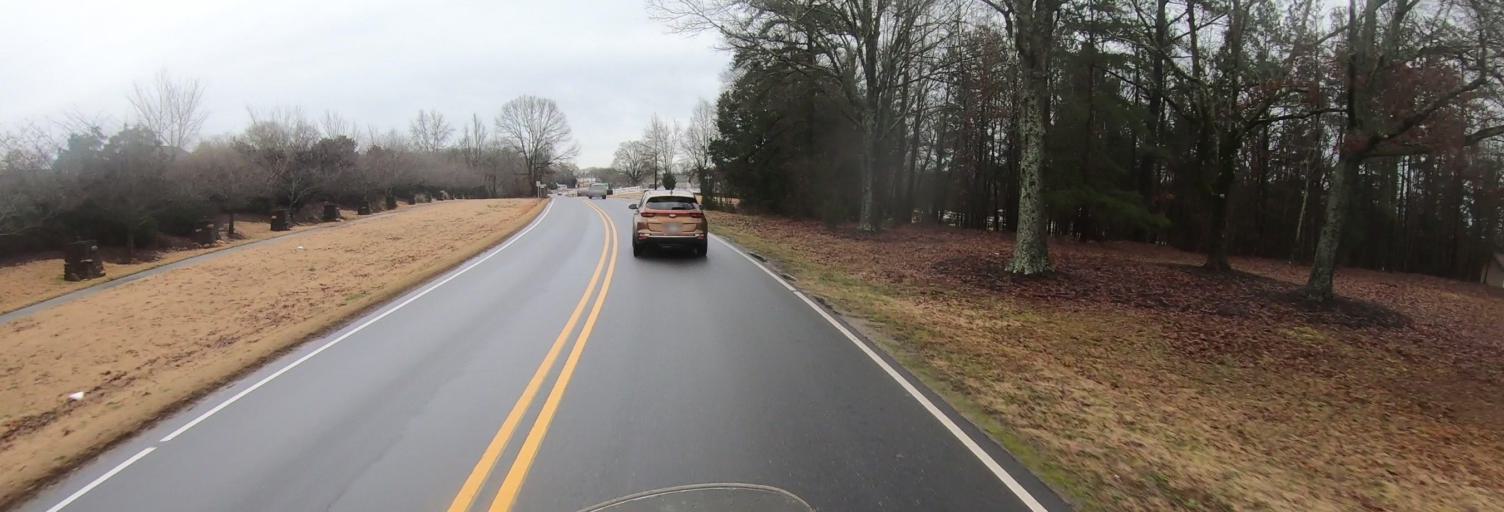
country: US
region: South Carolina
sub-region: York County
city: Tega Cay
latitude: 35.0702
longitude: -80.9994
